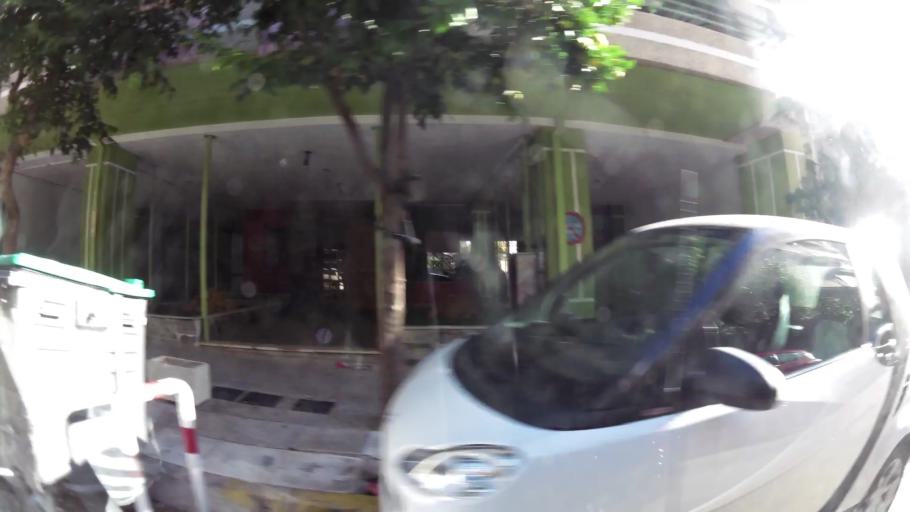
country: GR
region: Attica
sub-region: Nomos Piraios
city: Korydallos
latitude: 37.9774
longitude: 23.6525
